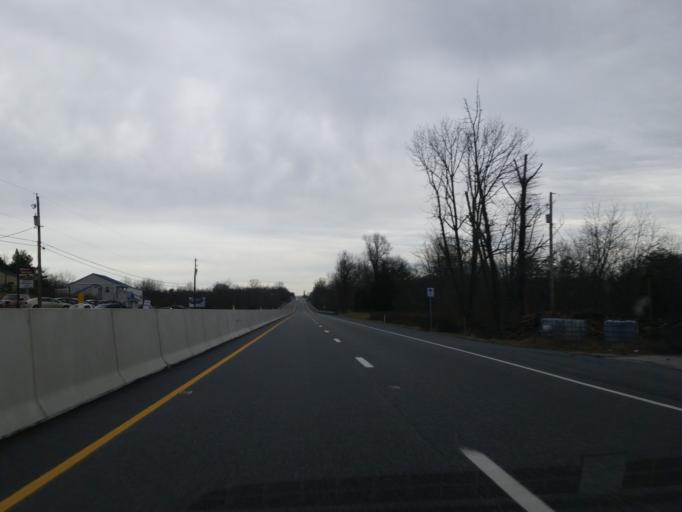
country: US
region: Pennsylvania
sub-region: Dauphin County
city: Skyline View
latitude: 40.3645
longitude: -76.6630
